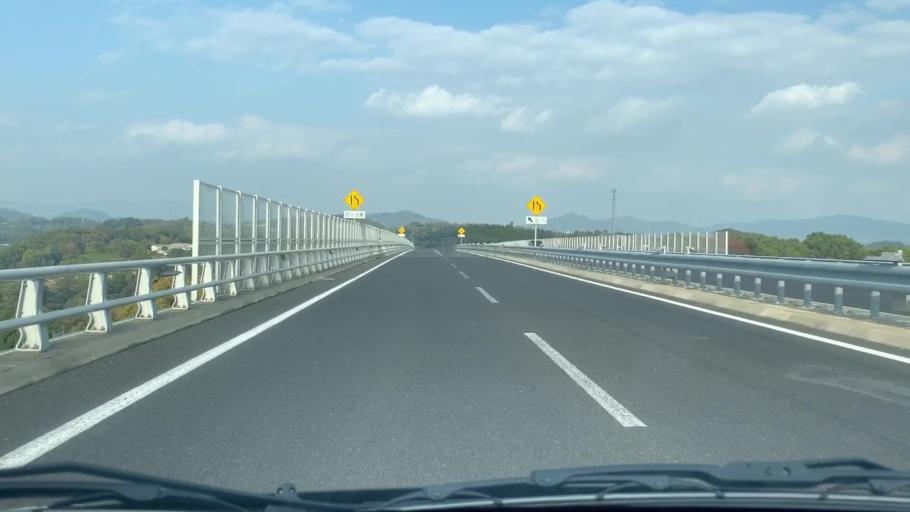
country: JP
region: Nagasaki
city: Sasebo
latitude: 33.0549
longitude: 129.7556
